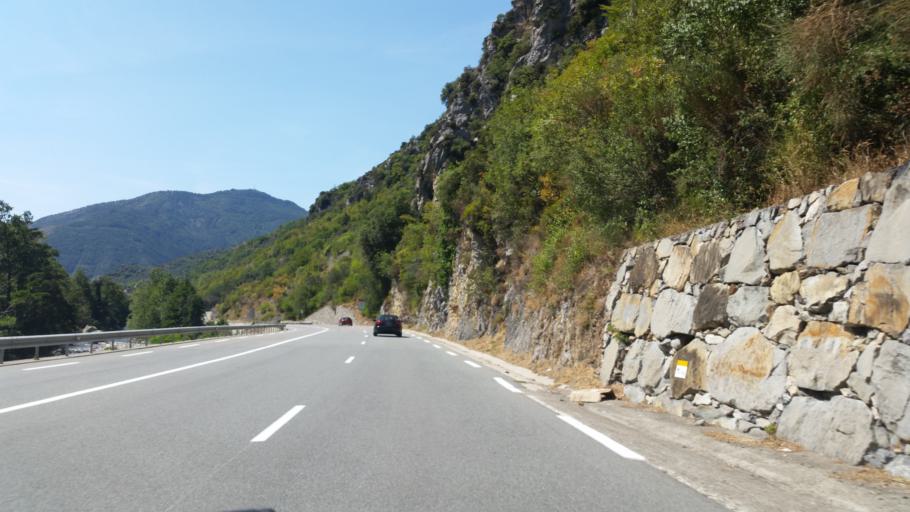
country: FR
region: Provence-Alpes-Cote d'Azur
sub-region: Departement des Alpes-Maritimes
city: Breil-sur-Roya
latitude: 43.9660
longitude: 7.5259
